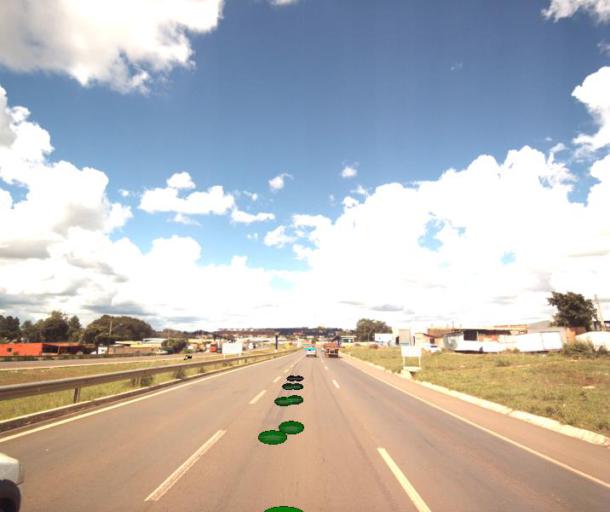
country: BR
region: Goias
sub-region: Anapolis
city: Anapolis
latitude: -16.3530
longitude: -48.9184
